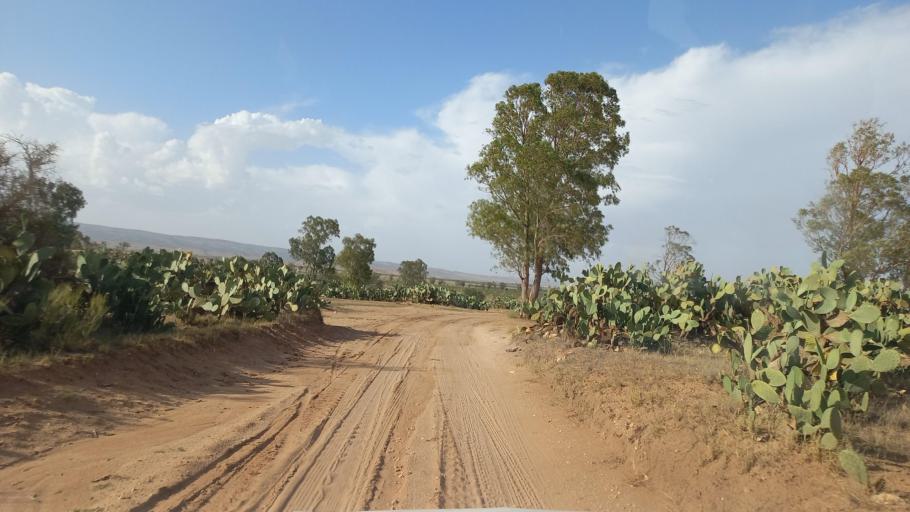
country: TN
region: Al Qasrayn
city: Kasserine
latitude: 35.2243
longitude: 8.9694
